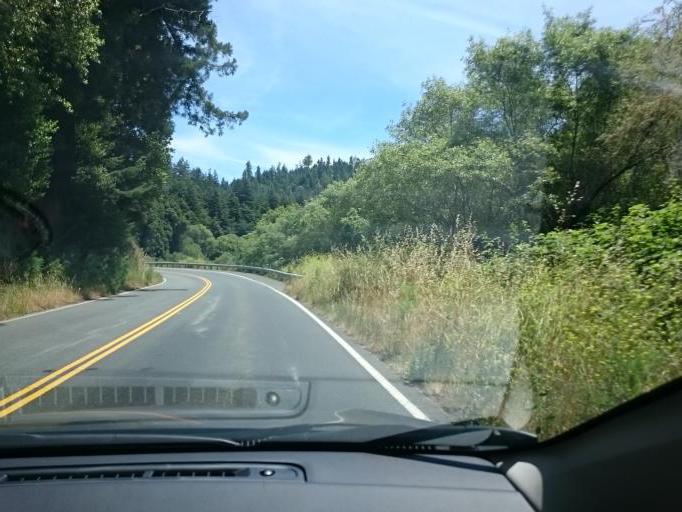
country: US
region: California
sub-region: Mendocino County
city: Fort Bragg
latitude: 39.1715
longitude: -123.6662
